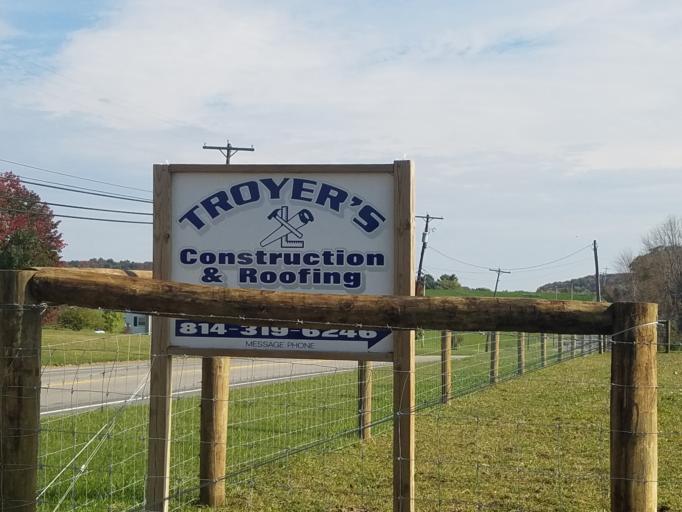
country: US
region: Pennsylvania
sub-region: Clarion County
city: Knox
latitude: 41.2340
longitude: -79.5690
